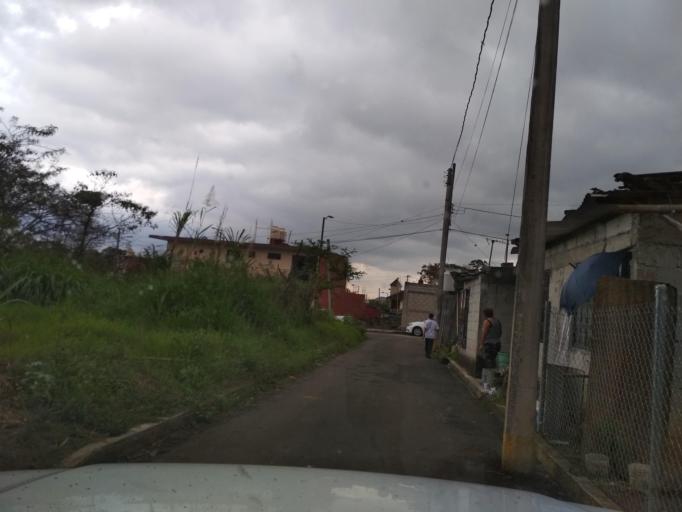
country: MX
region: Veracruz
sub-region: Cordoba
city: Veinte de Noviembre
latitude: 18.8728
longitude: -96.9528
